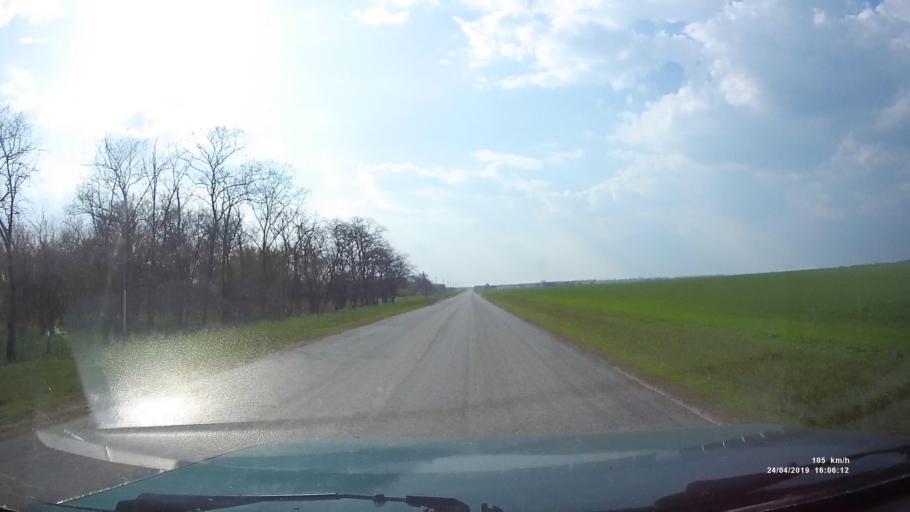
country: RU
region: Rostov
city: Sovetskoye
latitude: 46.6852
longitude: 42.3541
